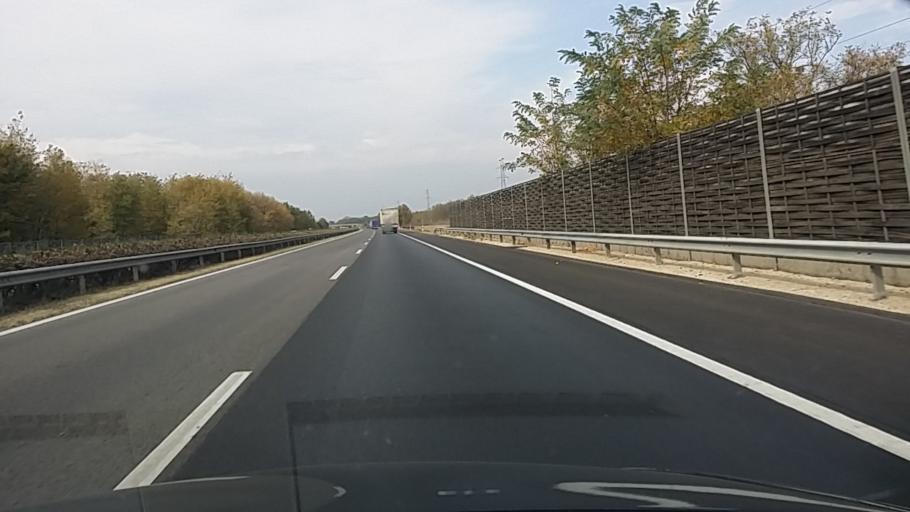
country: HU
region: Pest
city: Taborfalva
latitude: 47.1088
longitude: 19.5079
